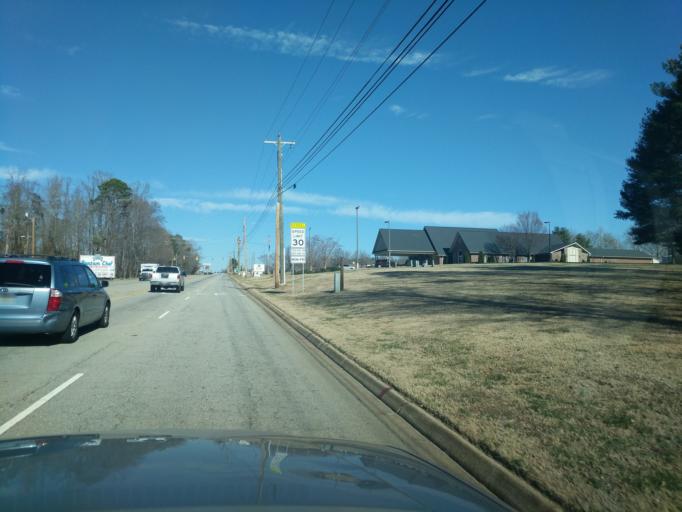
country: US
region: South Carolina
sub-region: Spartanburg County
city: Mayo
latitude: 35.1305
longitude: -81.8639
